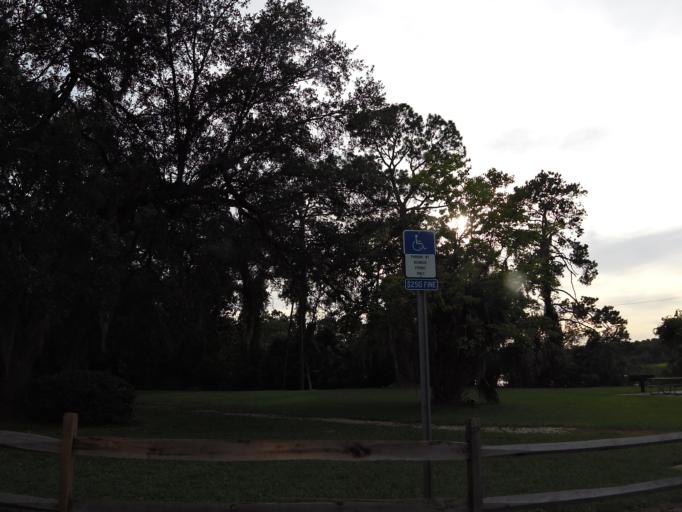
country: US
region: Florida
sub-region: Duval County
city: Jacksonville
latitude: 30.3985
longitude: -81.6985
